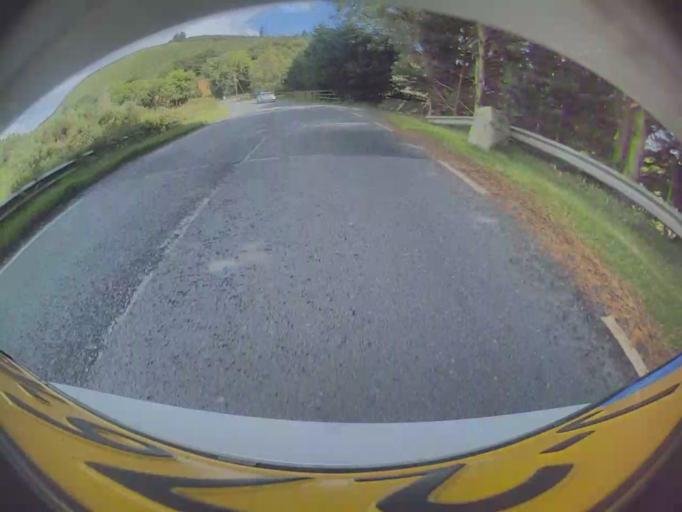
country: IE
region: Leinster
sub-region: Wicklow
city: Rathdrum
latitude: 53.0308
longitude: -6.2529
